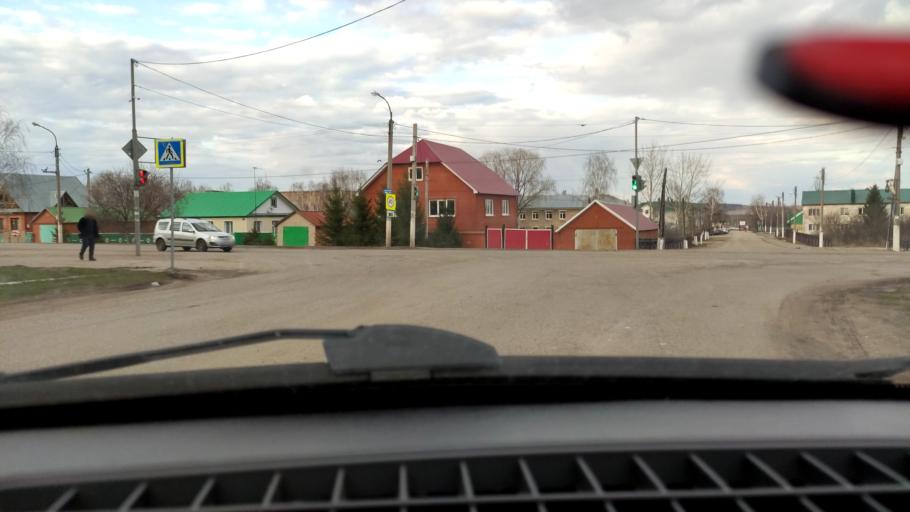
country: RU
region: Bashkortostan
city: Tolbazy
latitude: 54.0255
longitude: 55.8850
